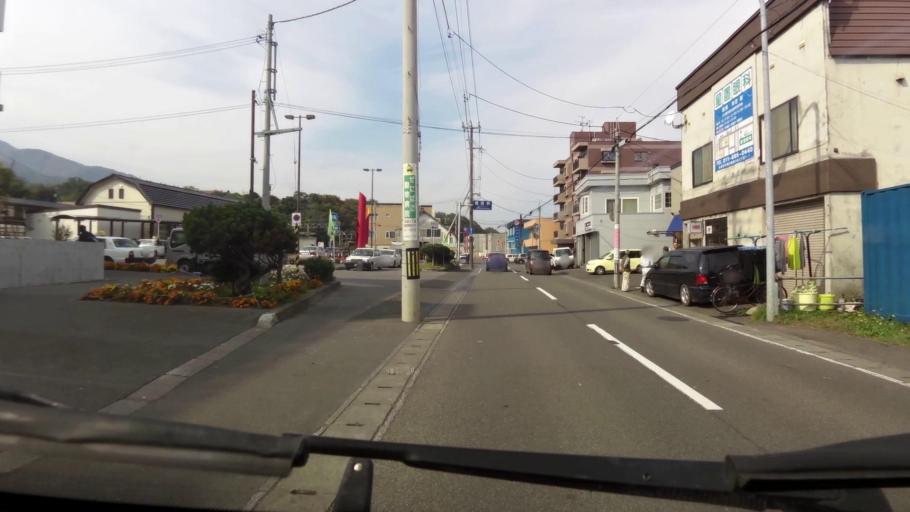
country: JP
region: Hokkaido
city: Otaru
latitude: 43.1438
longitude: 141.1601
